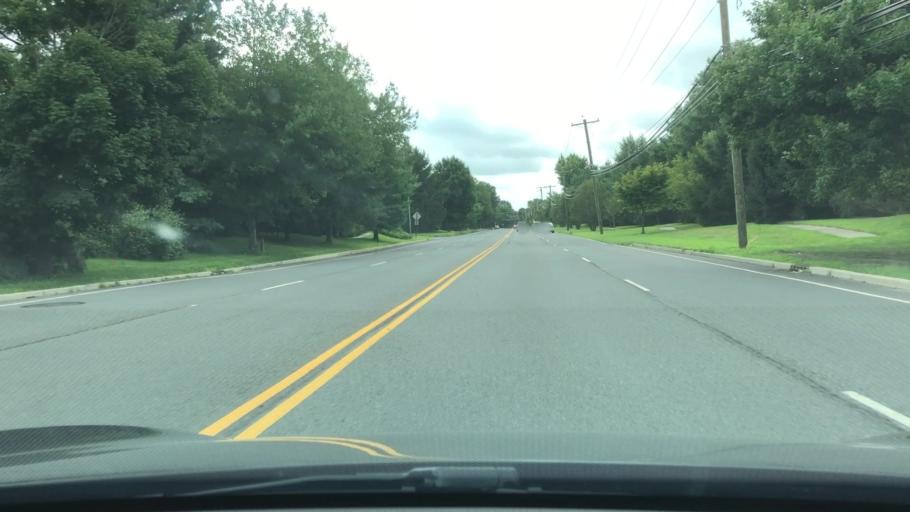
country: US
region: New Jersey
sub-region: Mercer County
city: Princeton Junction
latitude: 40.2943
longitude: -74.5912
